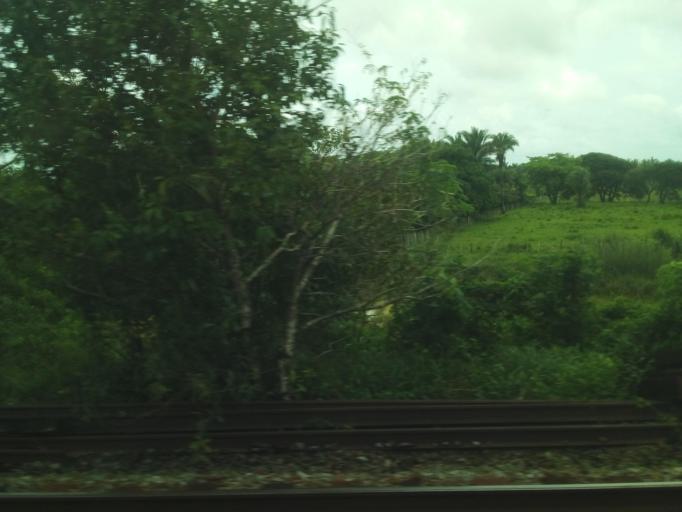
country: BR
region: Maranhao
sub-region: Arari
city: Arari
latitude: -3.5666
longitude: -44.8003
